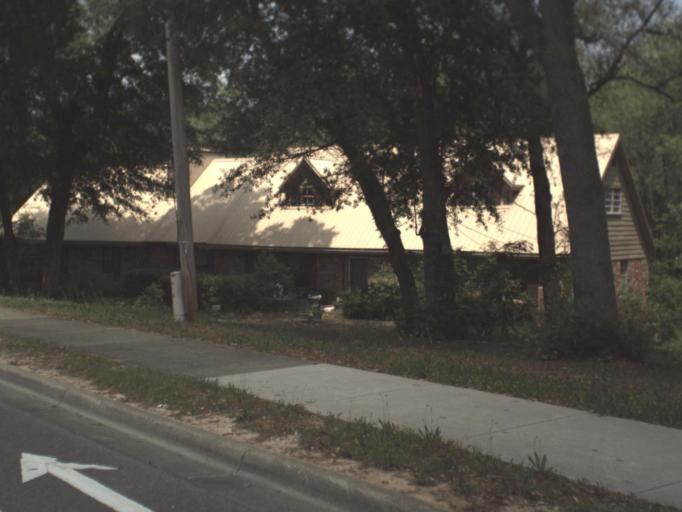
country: US
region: Florida
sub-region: Santa Rosa County
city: Milton
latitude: 30.6360
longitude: -87.0555
